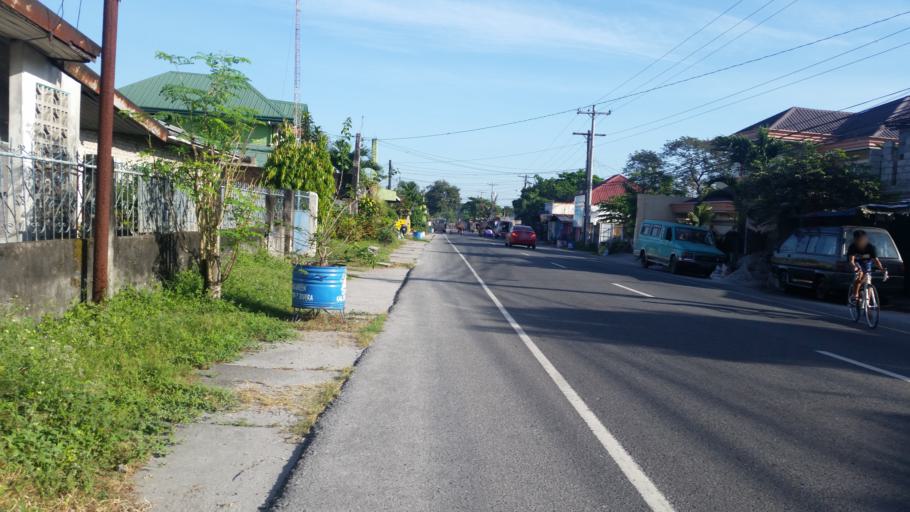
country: PH
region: Central Luzon
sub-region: Province of Pampanga
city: Mabalacat City
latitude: 15.2786
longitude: 120.5679
